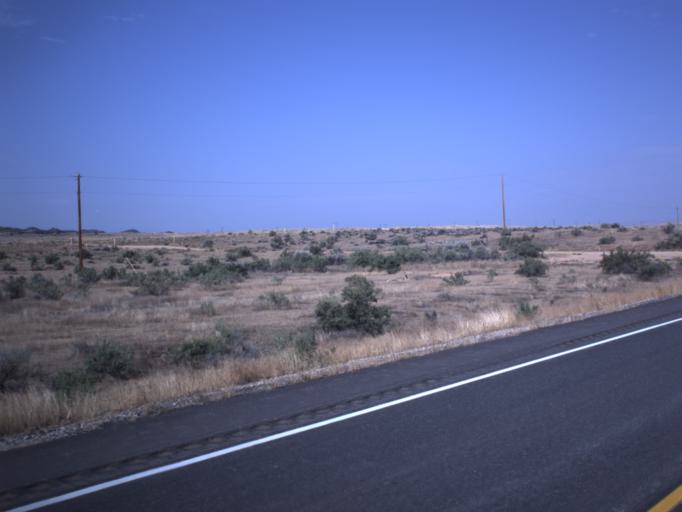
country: US
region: Utah
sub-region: Uintah County
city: Naples
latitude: 40.3084
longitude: -109.2162
